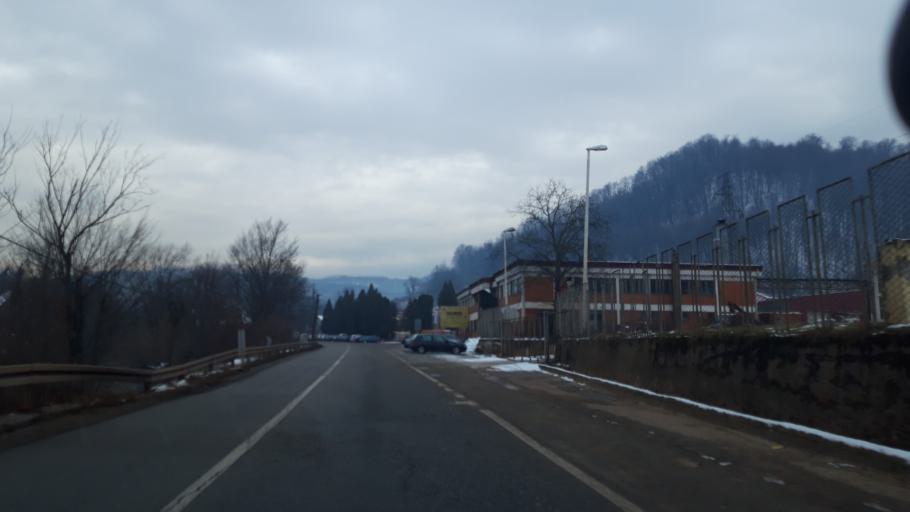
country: BA
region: Republika Srpska
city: Milici
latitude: 44.1770
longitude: 19.0739
